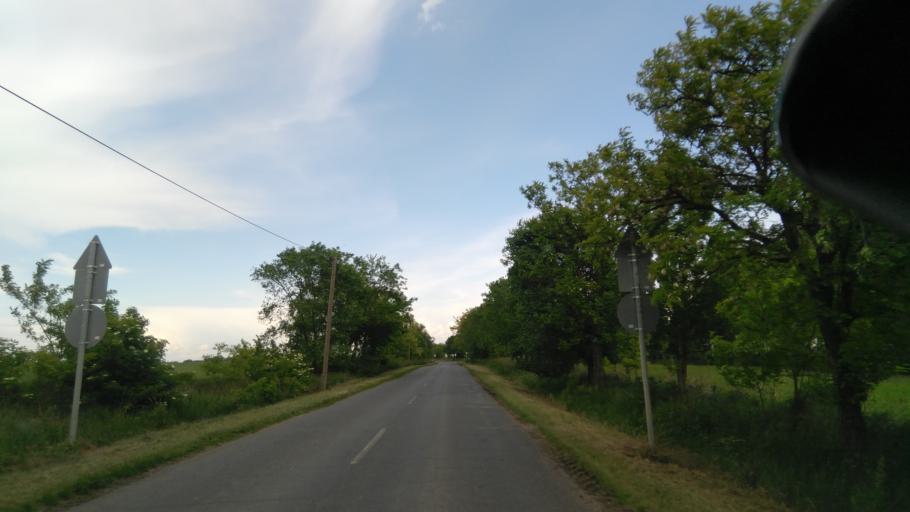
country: HU
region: Bekes
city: Dombegyhaz
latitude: 46.3492
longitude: 21.1553
